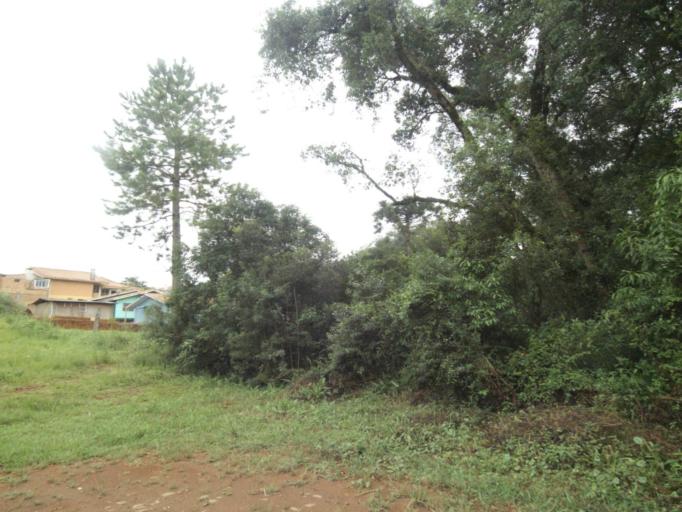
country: BR
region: Rio Grande do Sul
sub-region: Lagoa Vermelha
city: Lagoa Vermelha
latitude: -28.2159
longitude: -51.5293
